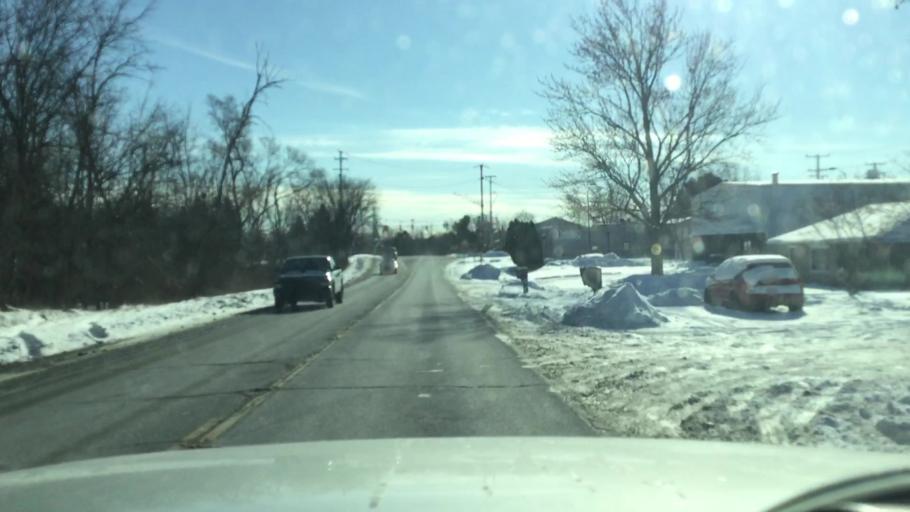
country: US
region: Michigan
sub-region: Oakland County
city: Keego Harbor
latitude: 42.6264
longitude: -83.3549
